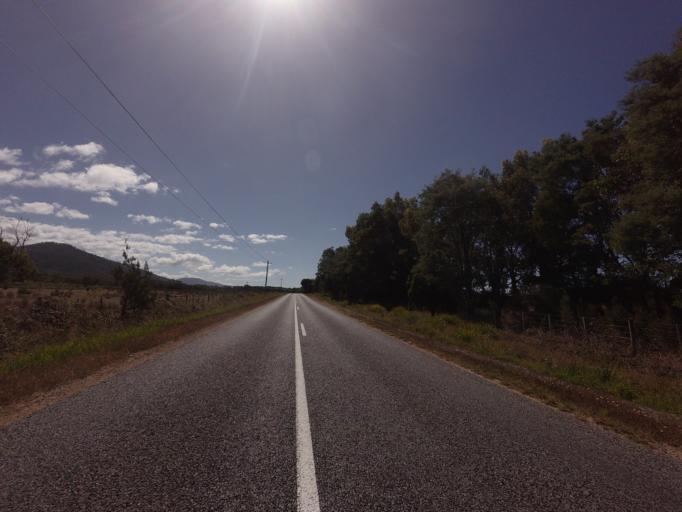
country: AU
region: Tasmania
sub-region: Break O'Day
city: St Helens
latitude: -41.7650
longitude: 148.2718
